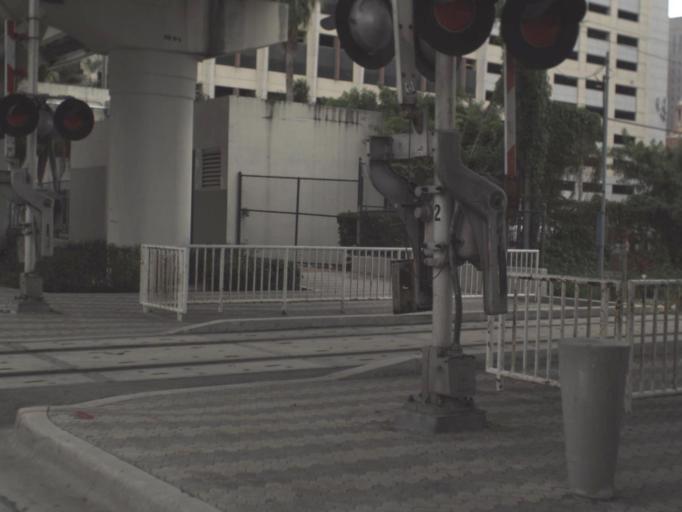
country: US
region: Florida
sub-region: Miami-Dade County
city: Miami
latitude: 25.7806
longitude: -80.1905
